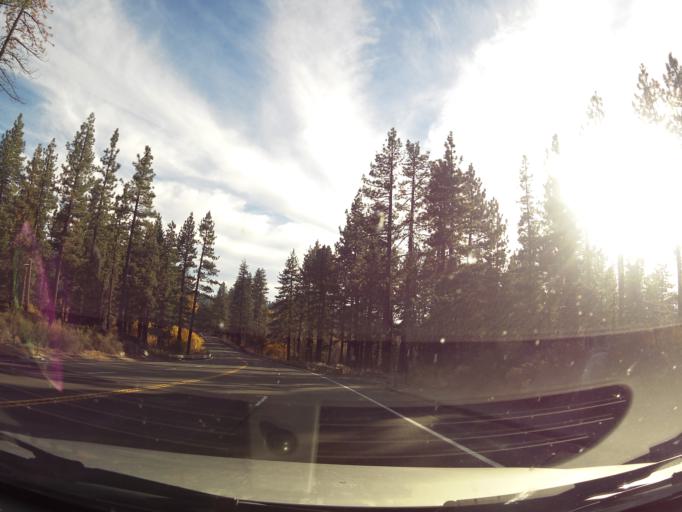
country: US
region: Nevada
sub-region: Douglas County
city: Kingsbury
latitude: 39.0167
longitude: -119.9475
